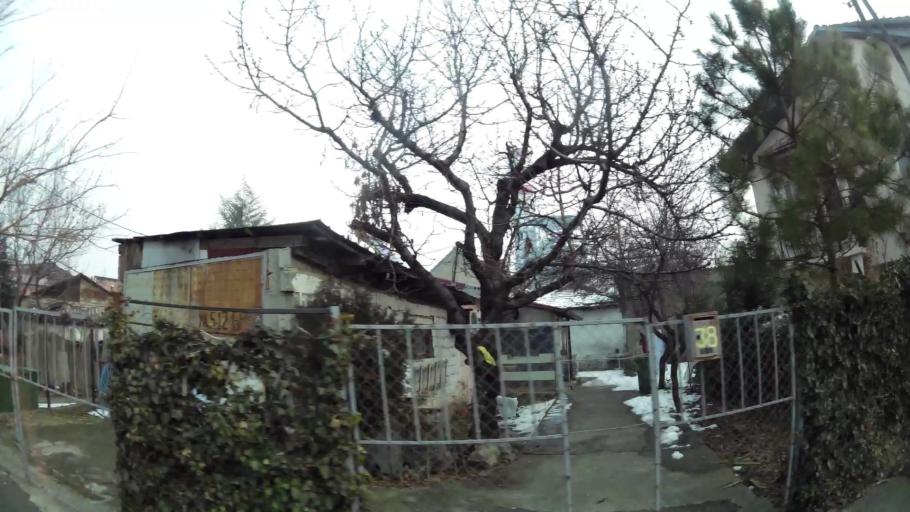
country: MK
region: Karpos
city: Skopje
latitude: 41.9941
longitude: 21.4513
